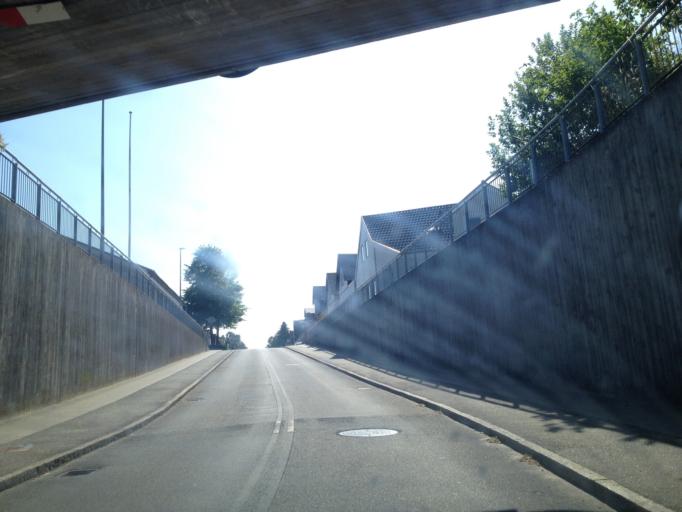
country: DK
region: South Denmark
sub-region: Haderslev Kommune
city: Vojens
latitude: 55.3138
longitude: 9.2874
